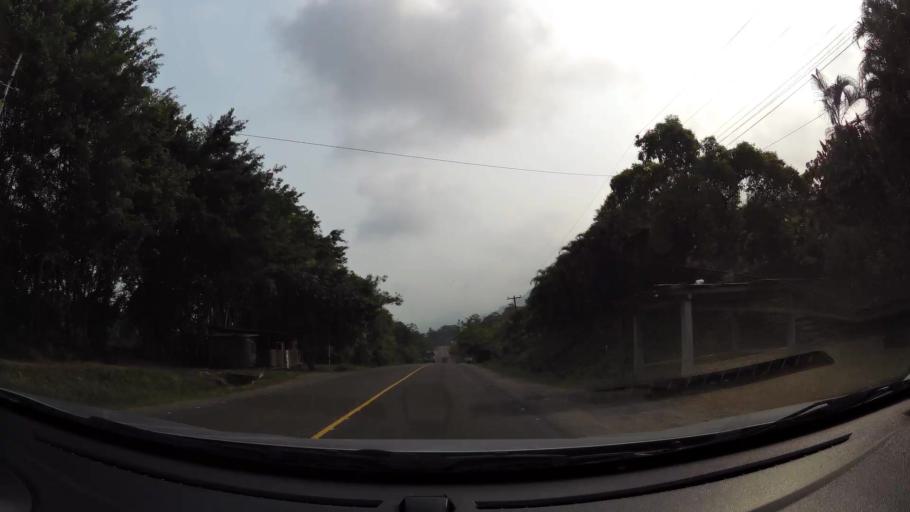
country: HN
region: Atlantida
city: Mezapa
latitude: 15.5806
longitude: -87.6134
